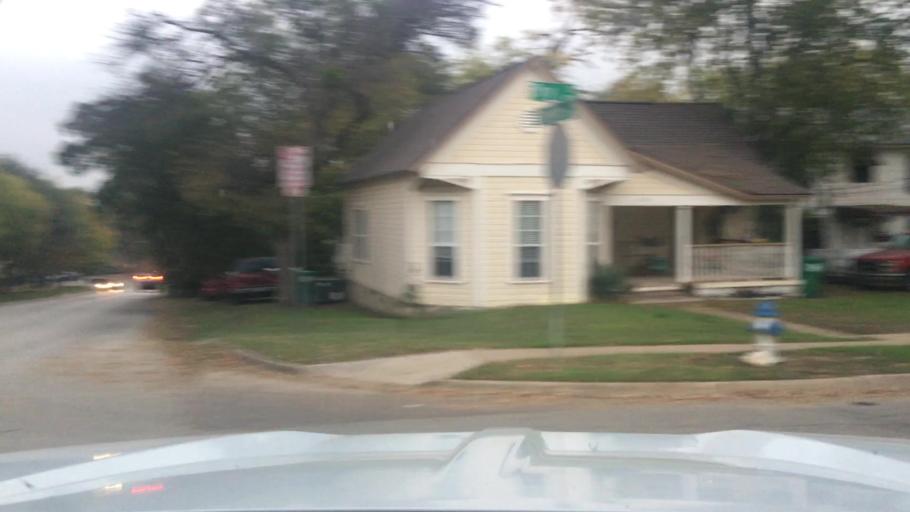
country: US
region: Texas
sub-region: Denton County
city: Denton
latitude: 33.2186
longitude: -97.1464
